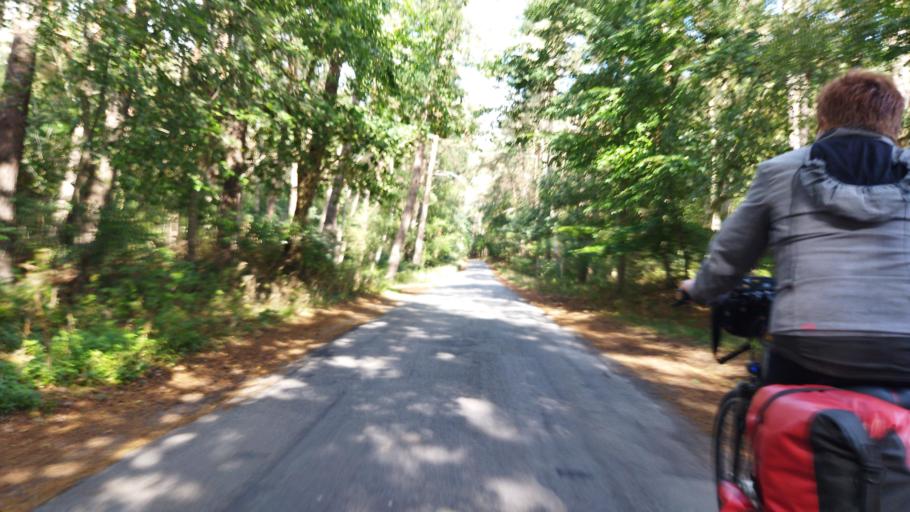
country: DE
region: Lower Saxony
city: Emsburen
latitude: 52.4237
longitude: 7.3430
